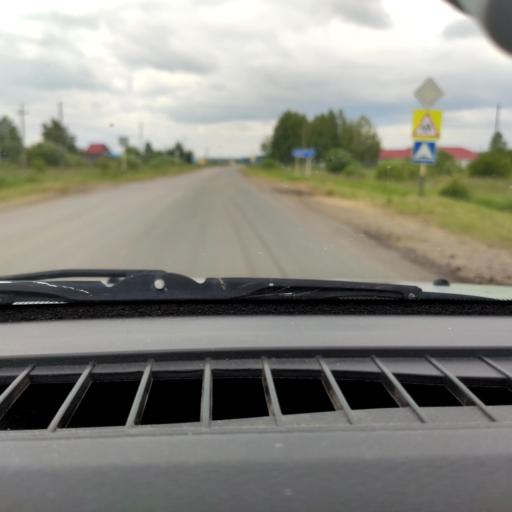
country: RU
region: Perm
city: Uinskoye
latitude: 57.0958
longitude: 56.6420
